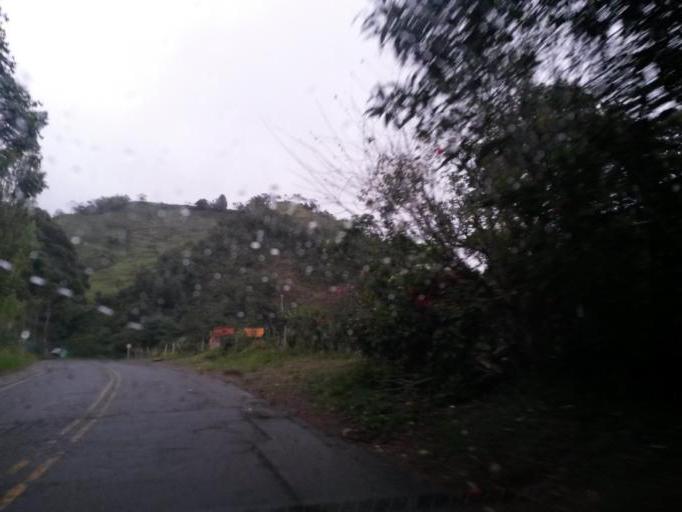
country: CO
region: Cauca
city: Popayan
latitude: 2.3997
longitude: -76.5011
